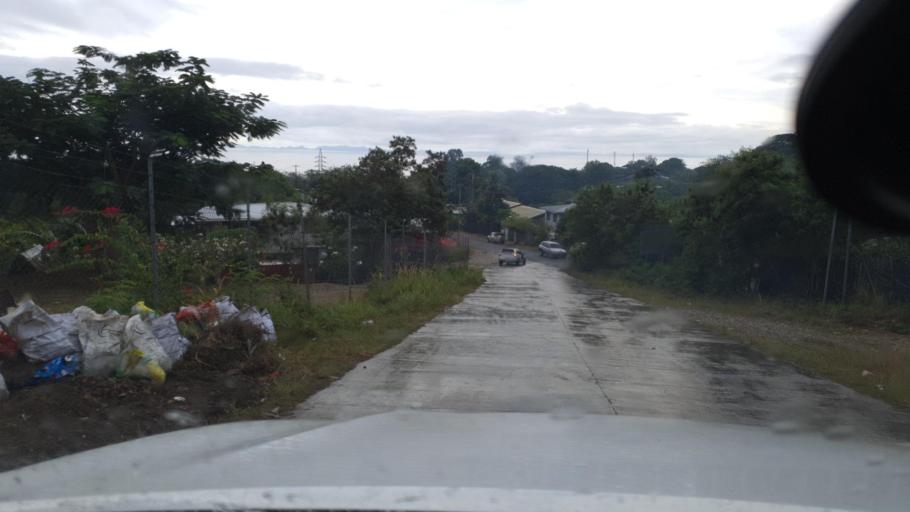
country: SB
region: Guadalcanal
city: Honiara
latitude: -9.4386
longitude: 159.9510
